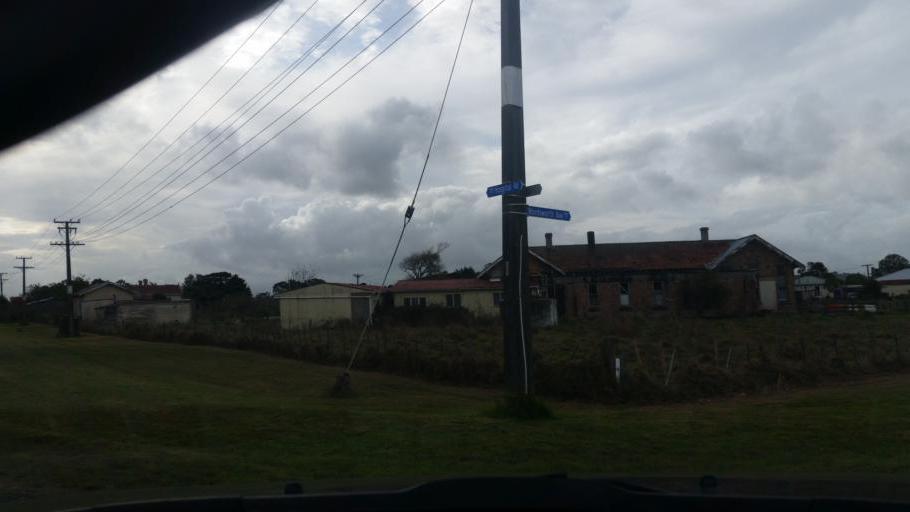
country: NZ
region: Northland
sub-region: Kaipara District
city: Dargaville
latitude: -36.0278
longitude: 173.9147
